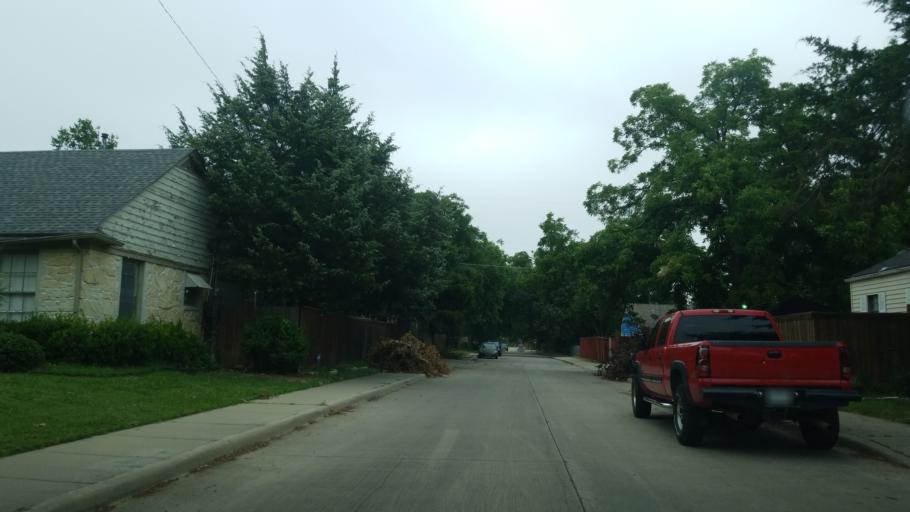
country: US
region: Texas
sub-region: Dallas County
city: University Park
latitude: 32.8368
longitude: -96.8591
